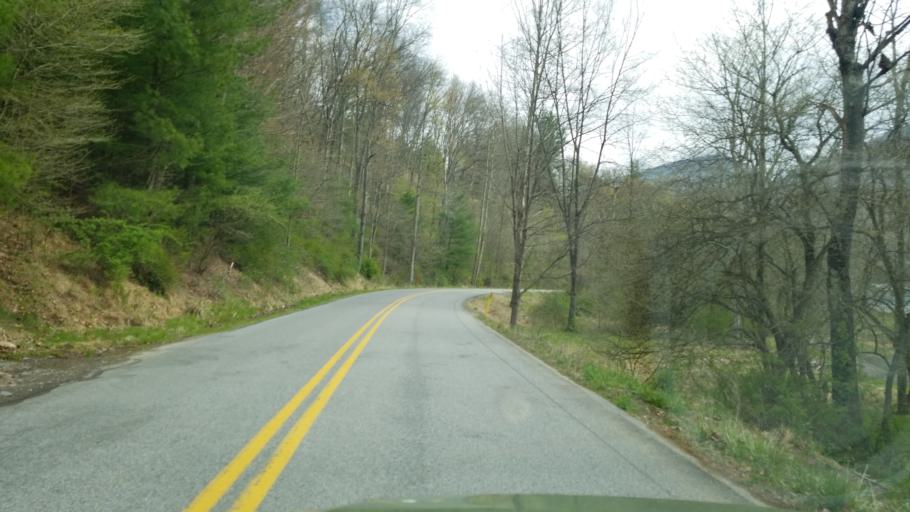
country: US
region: Pennsylvania
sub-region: Cameron County
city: Emporium
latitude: 41.3124
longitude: -78.0845
